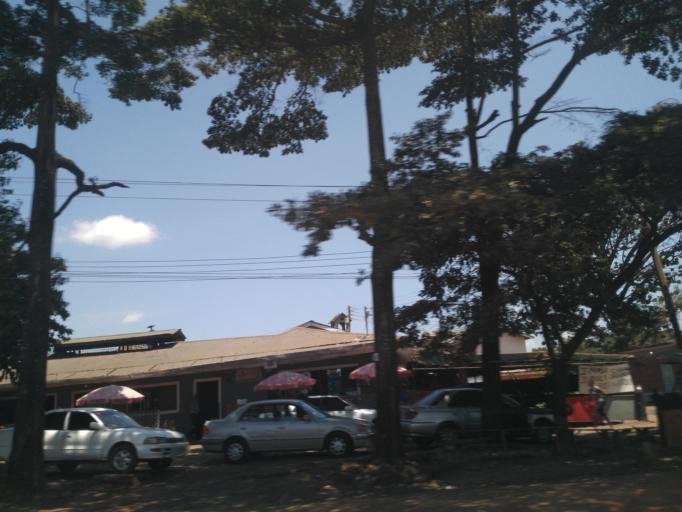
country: TZ
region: Arusha
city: Arusha
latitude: -3.3717
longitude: 36.6748
